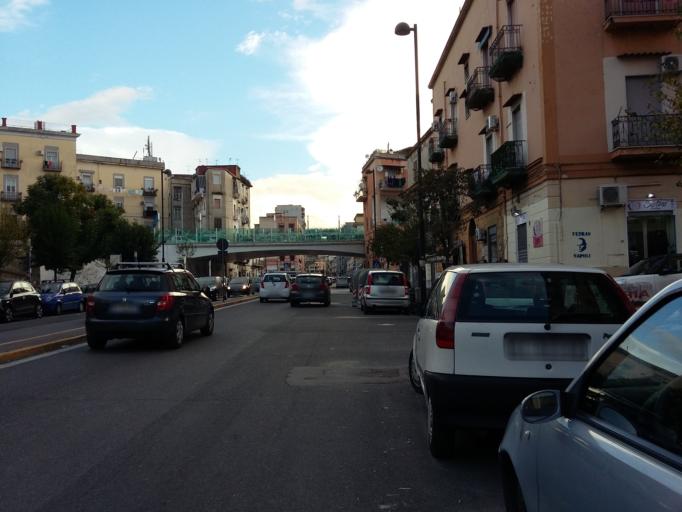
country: IT
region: Campania
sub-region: Provincia di Napoli
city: Napoli
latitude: 40.8641
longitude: 14.2696
